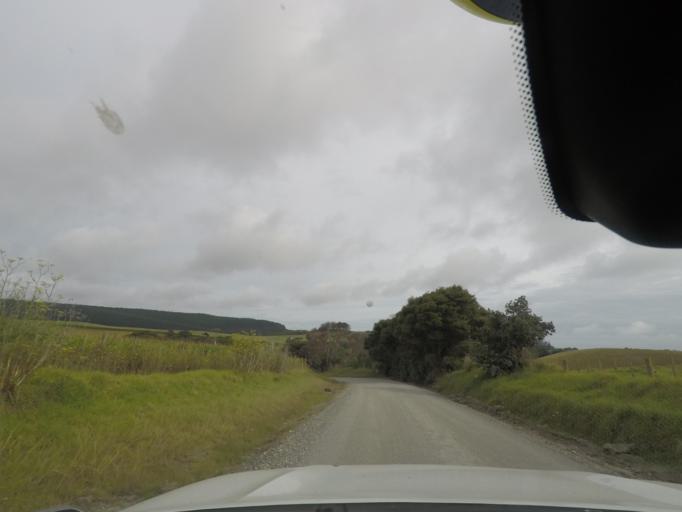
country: NZ
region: Auckland
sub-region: Auckland
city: Parakai
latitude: -36.4733
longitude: 174.2574
